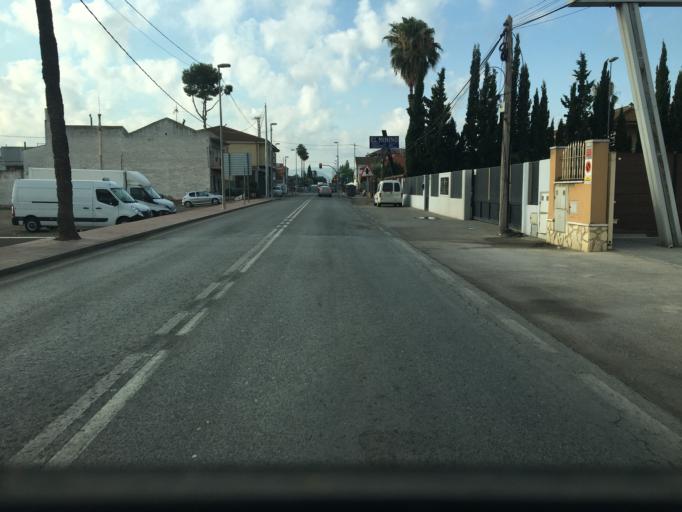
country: ES
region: Murcia
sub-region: Murcia
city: Santomera
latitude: 38.0334
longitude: -1.0429
